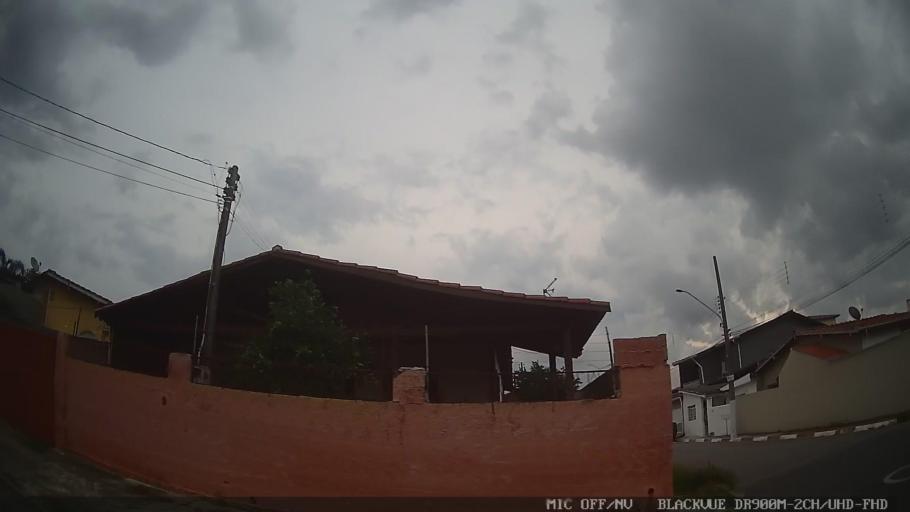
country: BR
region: Sao Paulo
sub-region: Atibaia
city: Atibaia
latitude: -23.1240
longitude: -46.5576
